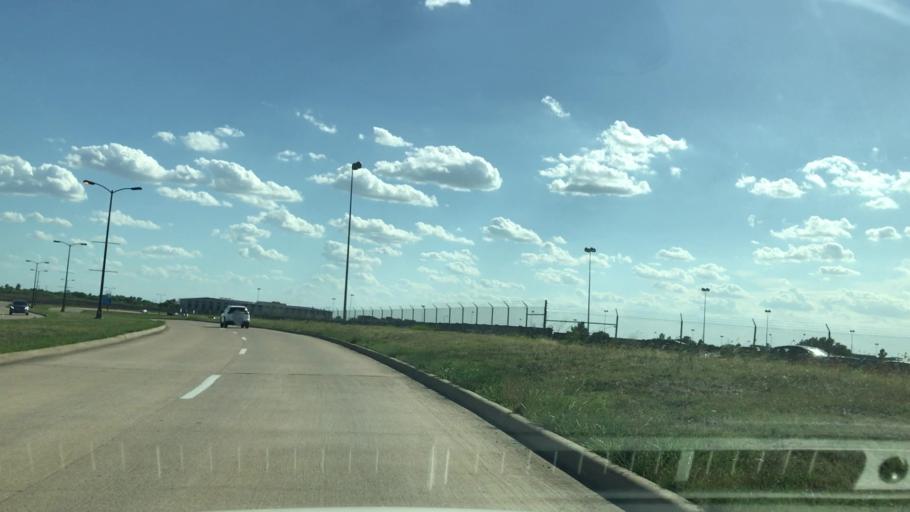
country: US
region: Texas
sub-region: Tarrant County
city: Euless
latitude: 32.8565
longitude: -97.0253
